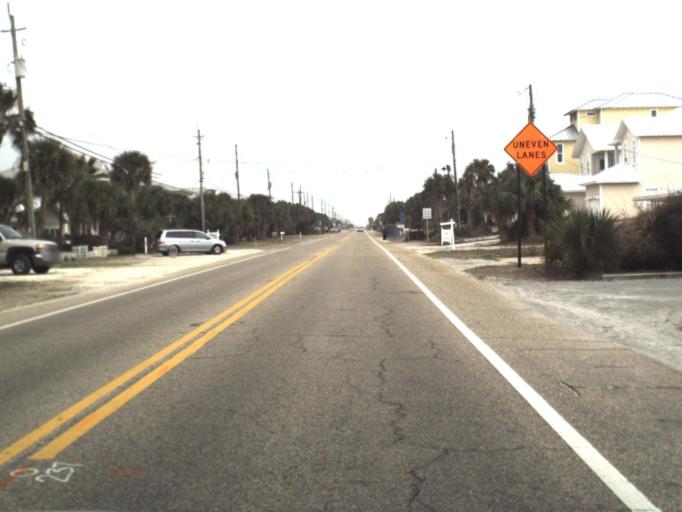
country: US
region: Florida
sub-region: Bay County
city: Laguna Beach
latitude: 30.2462
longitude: -85.9391
